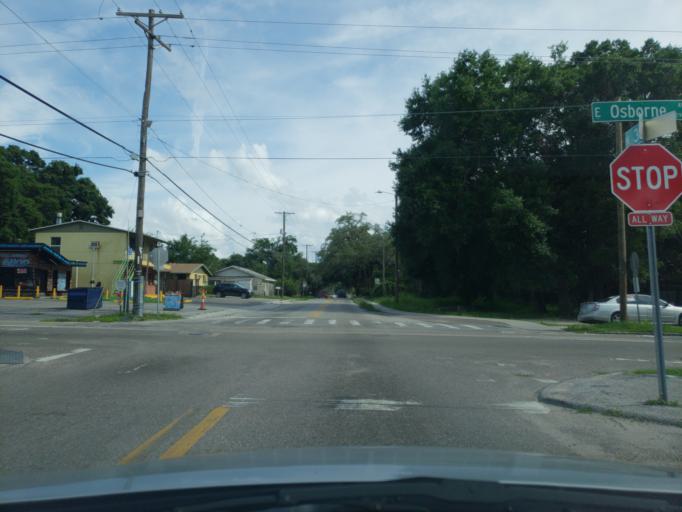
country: US
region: Florida
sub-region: Hillsborough County
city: East Lake-Orient Park
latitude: 27.9889
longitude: -82.4265
